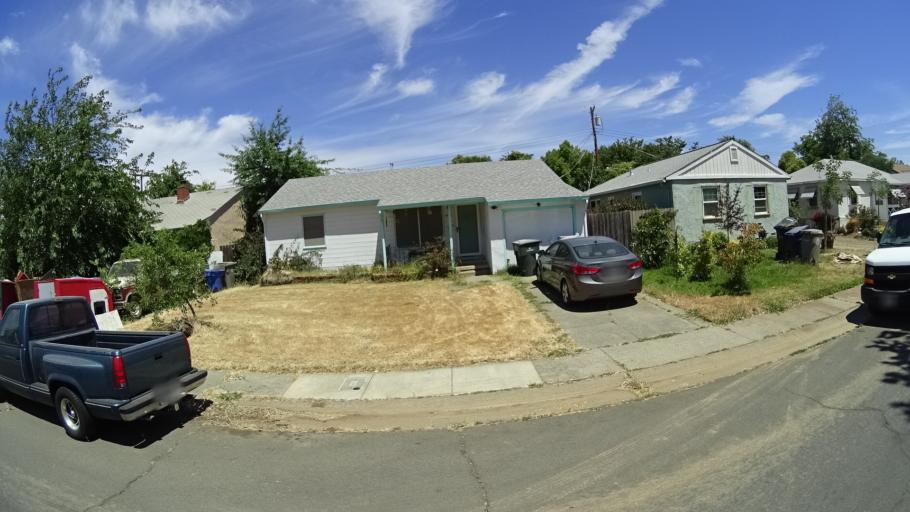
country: US
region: California
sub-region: Sacramento County
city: Parkway
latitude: 38.5181
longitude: -121.4350
